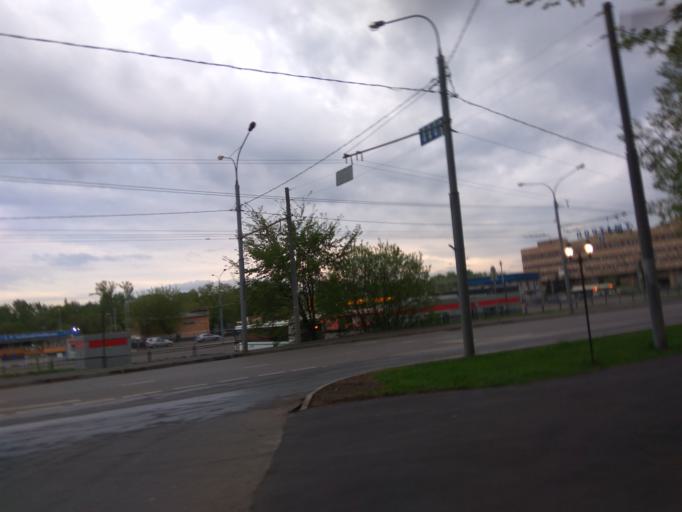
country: RU
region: Moskovskaya
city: Novogireyevo
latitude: 55.7450
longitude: 37.8117
